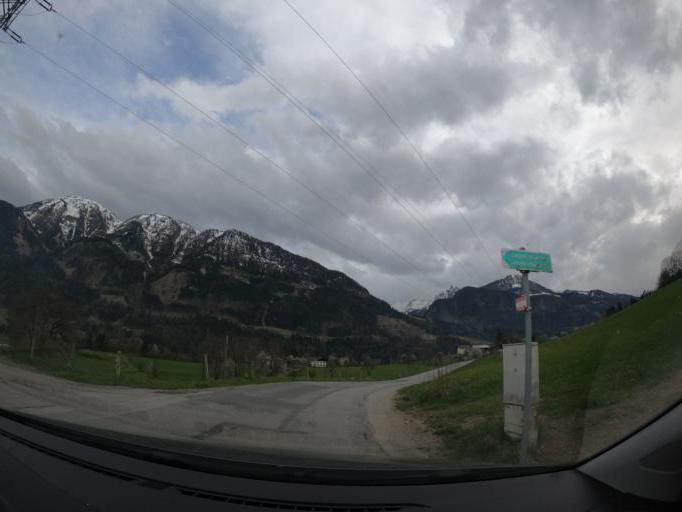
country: AT
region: Salzburg
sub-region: Politischer Bezirk Sankt Johann im Pongau
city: Goldegg
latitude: 47.3066
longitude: 13.0885
